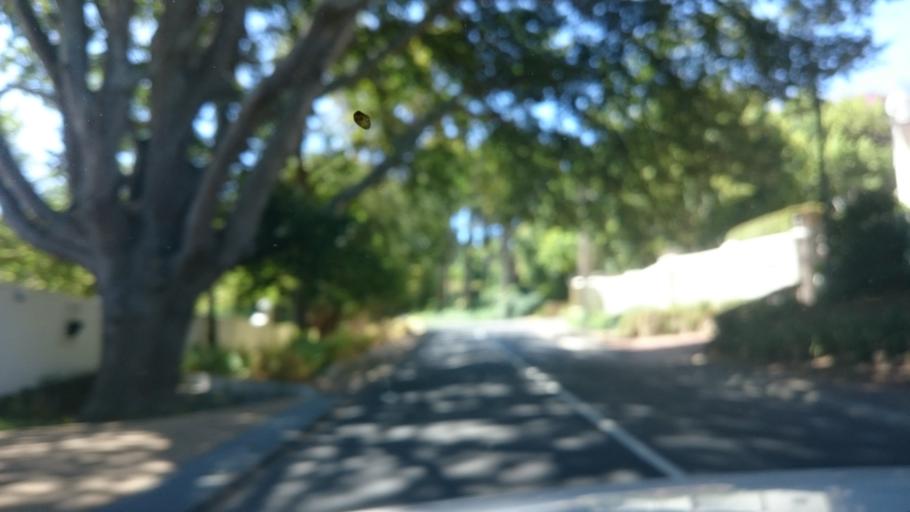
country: ZA
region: Western Cape
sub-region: City of Cape Town
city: Newlands
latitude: -33.9981
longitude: 18.4475
